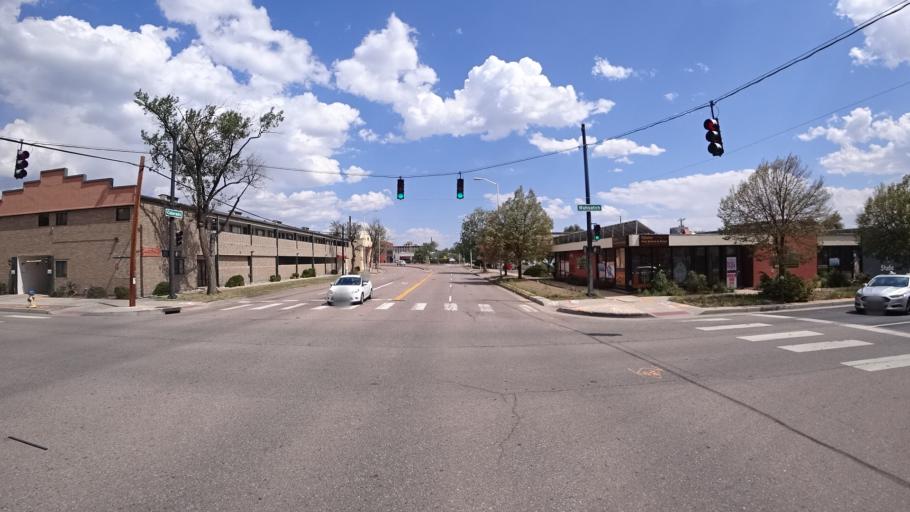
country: US
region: Colorado
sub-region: El Paso County
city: Colorado Springs
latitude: 38.8323
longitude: -104.8181
